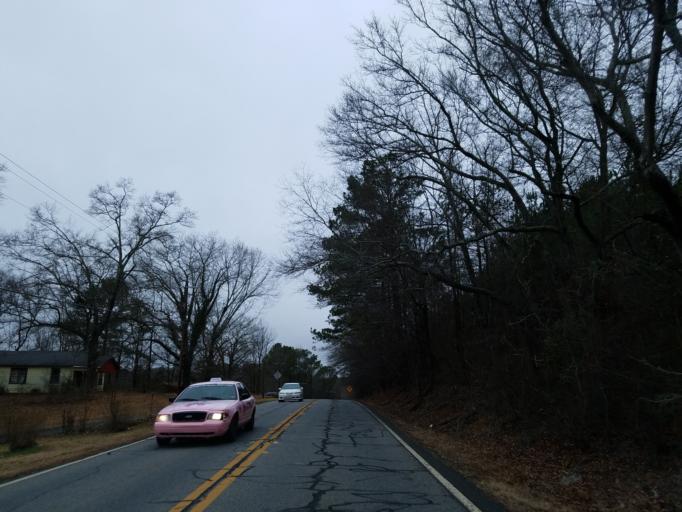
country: US
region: Georgia
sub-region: Bartow County
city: Cartersville
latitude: 34.2135
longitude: -84.8380
